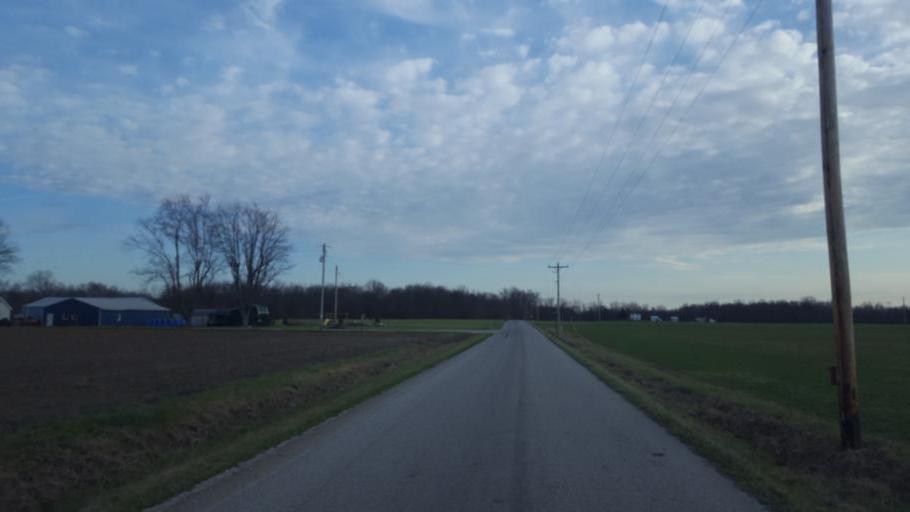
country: US
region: Ohio
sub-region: Crawford County
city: Bucyrus
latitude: 40.6671
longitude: -82.9483
